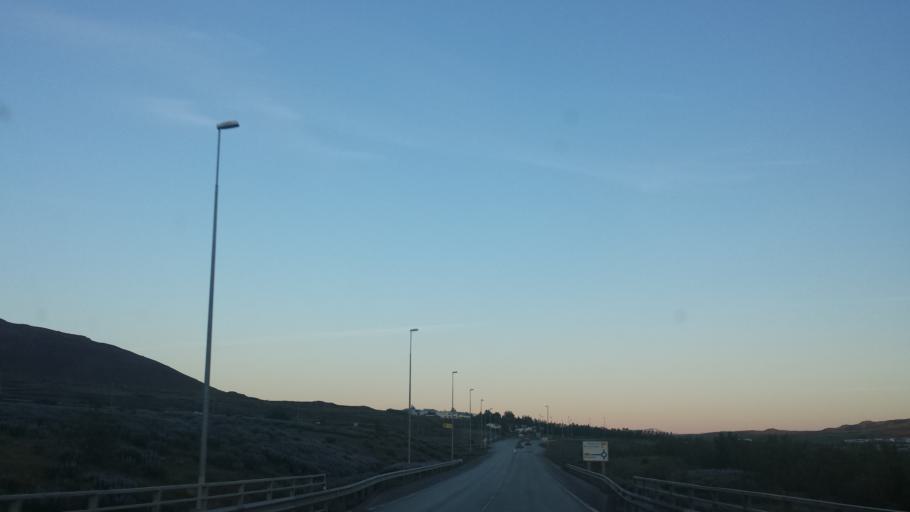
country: IS
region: Capital Region
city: Mosfellsbaer
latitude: 64.1803
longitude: -21.6786
